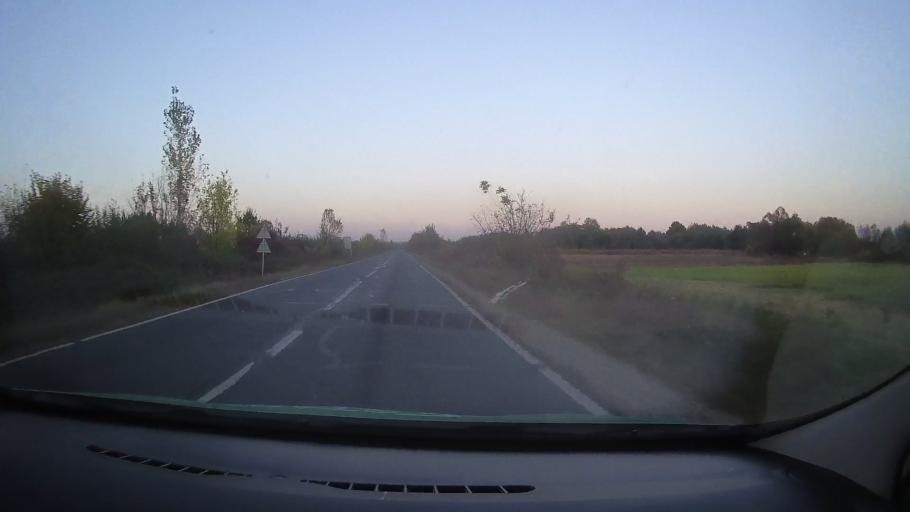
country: RO
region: Timis
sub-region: Comuna Dumbrava
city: Dumbrava
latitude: 45.8413
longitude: 22.1453
